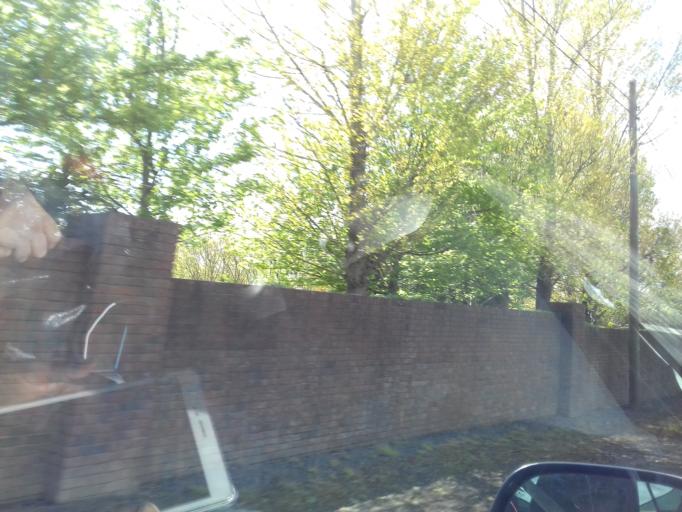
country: IE
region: Leinster
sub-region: Loch Garman
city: Castlebridge
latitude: 52.3740
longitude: -6.4330
